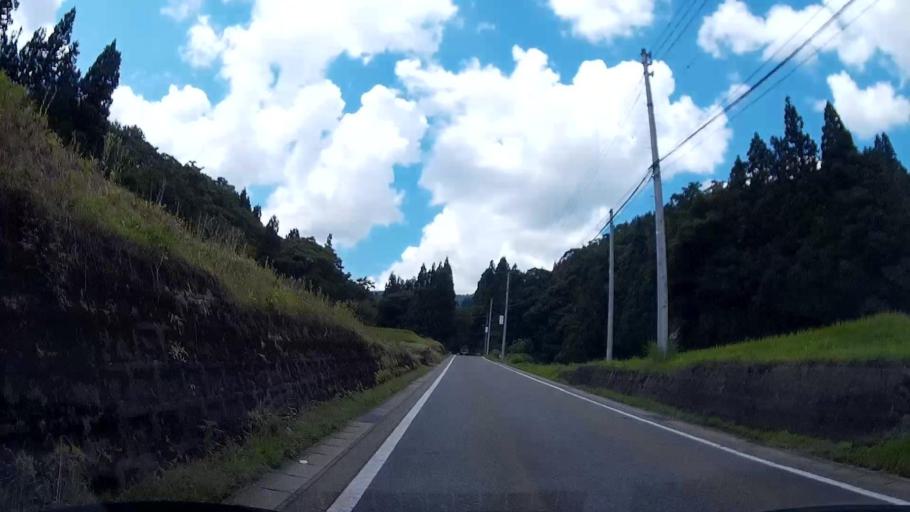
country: JP
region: Niigata
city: Shiozawa
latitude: 37.0190
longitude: 138.8184
